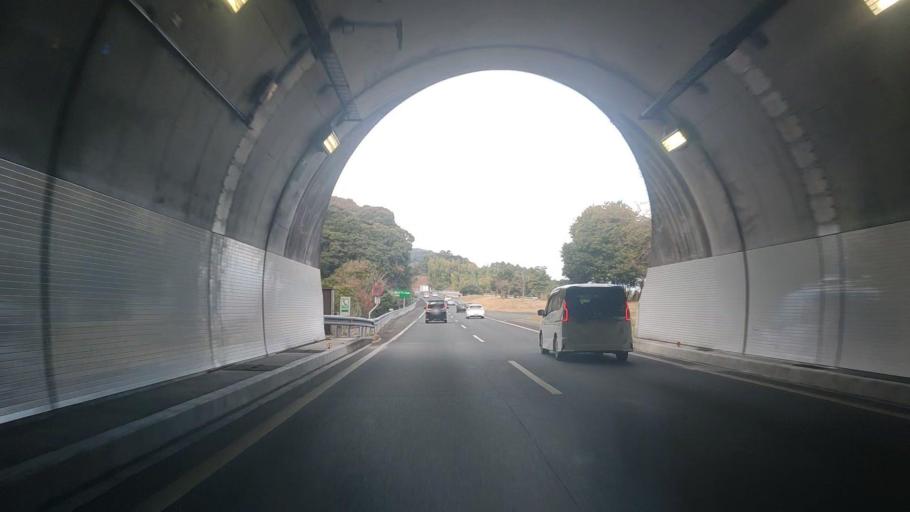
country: JP
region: Fukuoka
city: Kitakyushu
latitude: 33.8128
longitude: 130.9076
